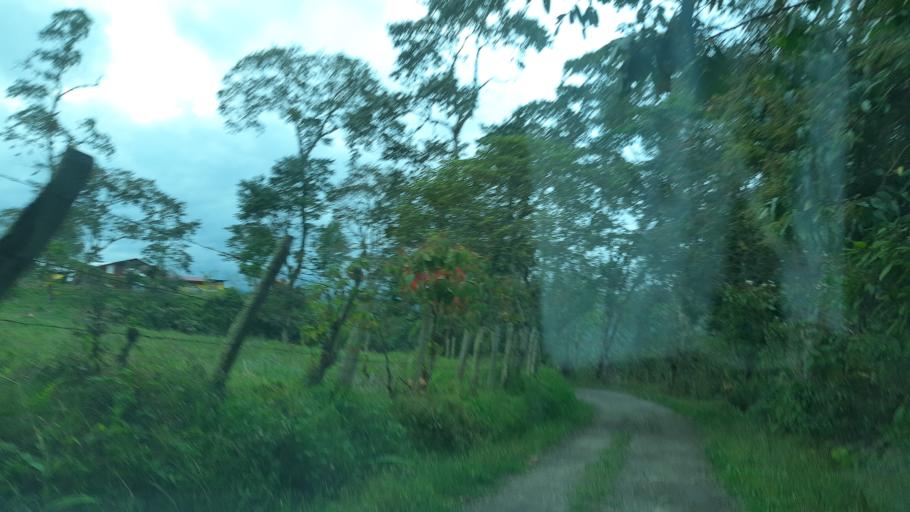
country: CO
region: Boyaca
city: Garagoa
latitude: 5.0821
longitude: -73.3495
